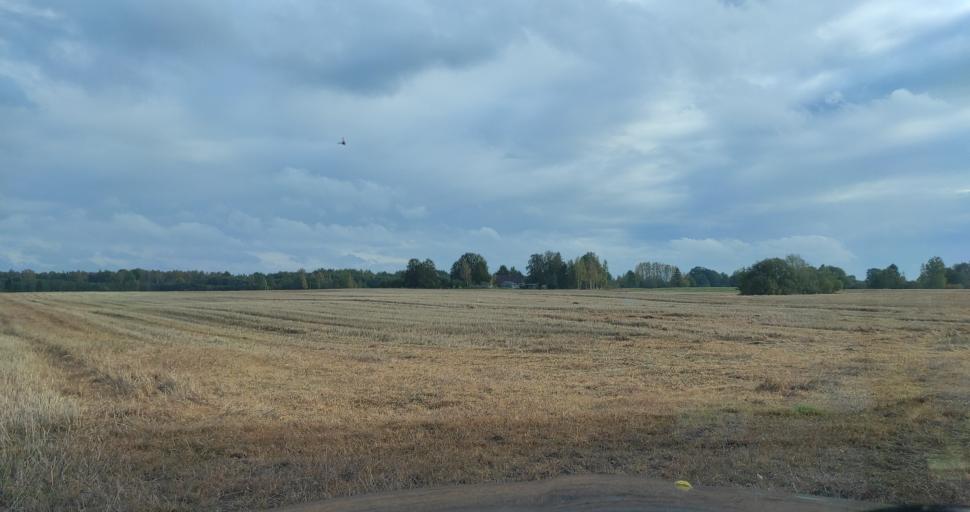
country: LV
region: Talsu Rajons
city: Sabile
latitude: 56.9011
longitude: 22.4214
